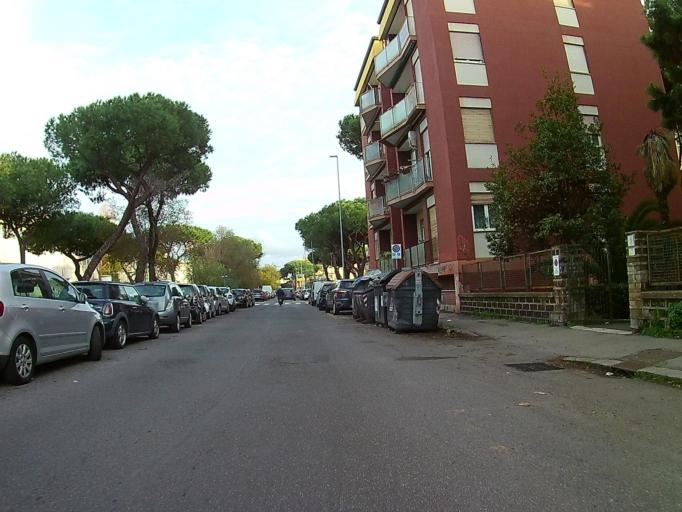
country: IT
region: Latium
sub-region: Citta metropolitana di Roma Capitale
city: Lido di Ostia
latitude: 41.7361
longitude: 12.2858
